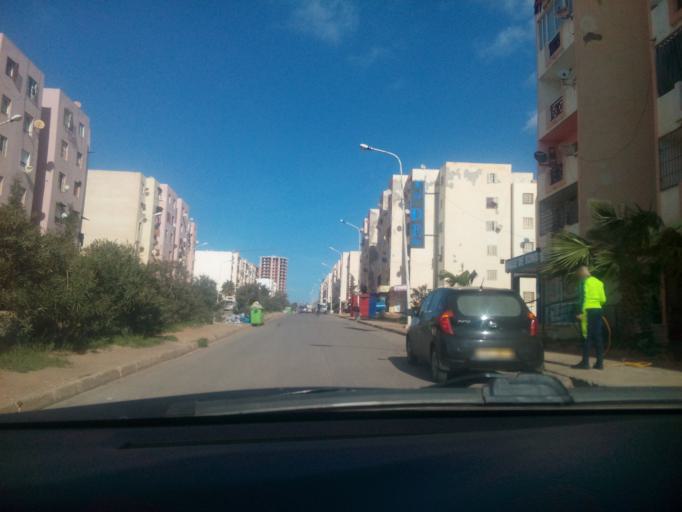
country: DZ
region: Oran
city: Bir el Djir
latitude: 35.7040
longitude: -0.5639
